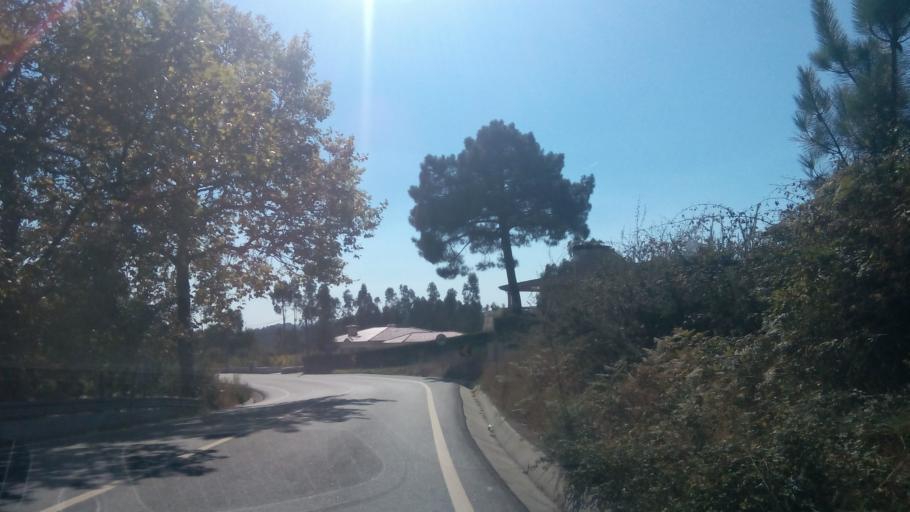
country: PT
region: Porto
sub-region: Amarante
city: Figueiro
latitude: 41.2740
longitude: -8.2088
